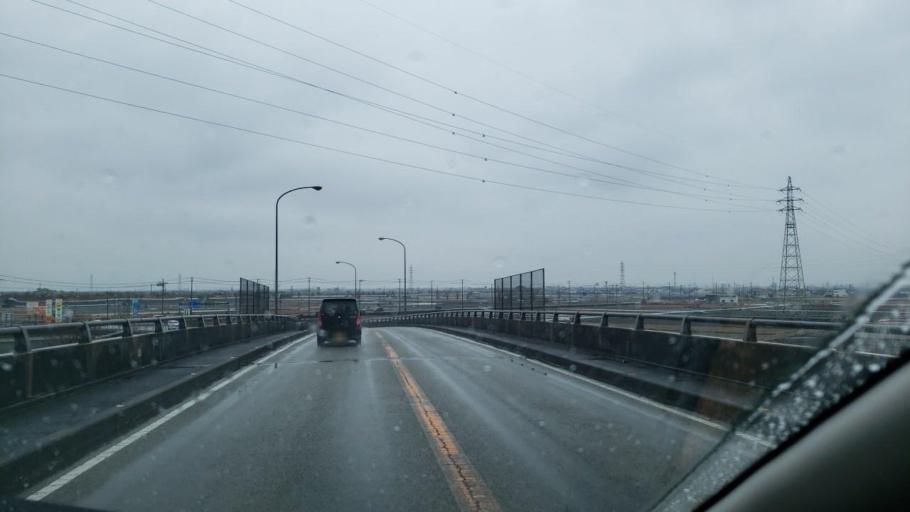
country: JP
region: Tokushima
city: Narutocho-mitsuishi
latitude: 34.1613
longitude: 134.5545
